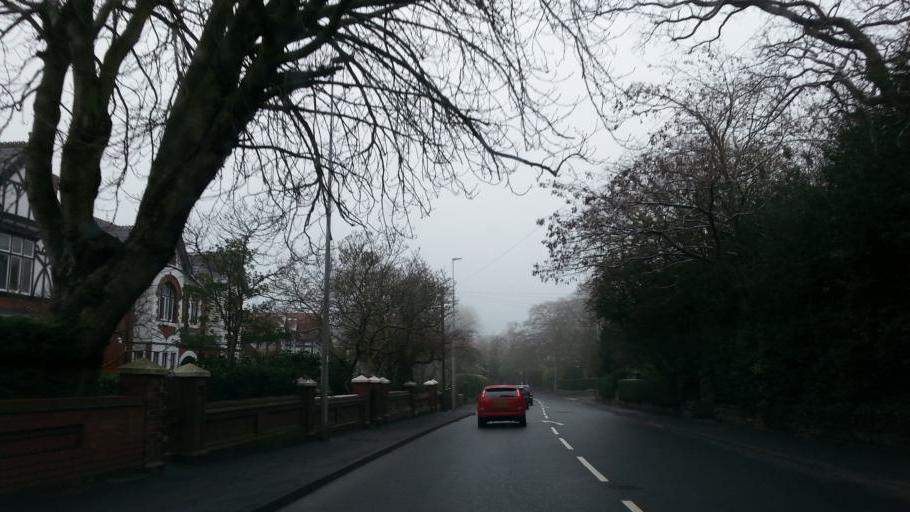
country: GB
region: England
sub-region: Cheshire East
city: Congleton
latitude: 53.1587
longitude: -2.1946
